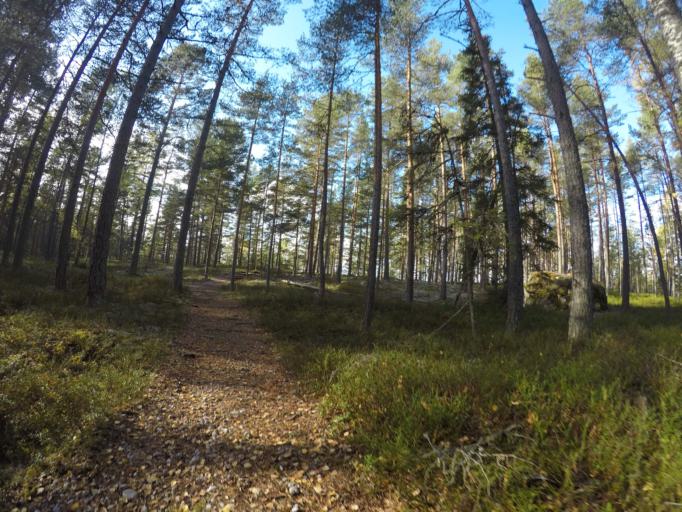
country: SE
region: Vaestmanland
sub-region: Kungsors Kommun
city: Kungsoer
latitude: 59.3169
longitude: 16.1143
